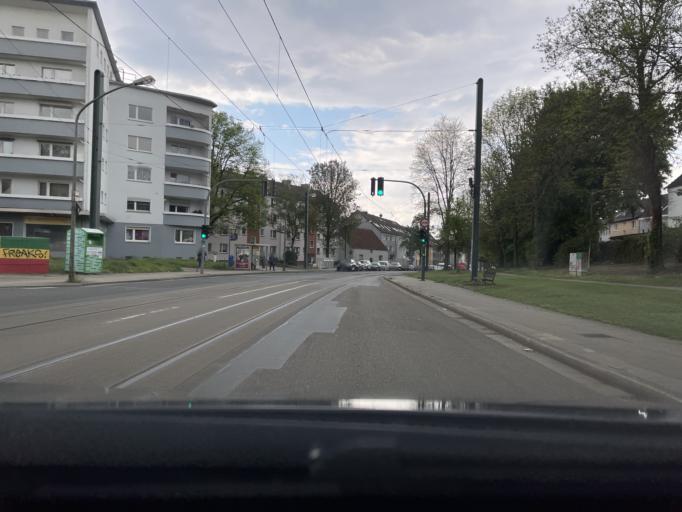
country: DE
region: North Rhine-Westphalia
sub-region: Regierungsbezirk Dusseldorf
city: Essen
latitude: 51.4728
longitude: 6.9774
